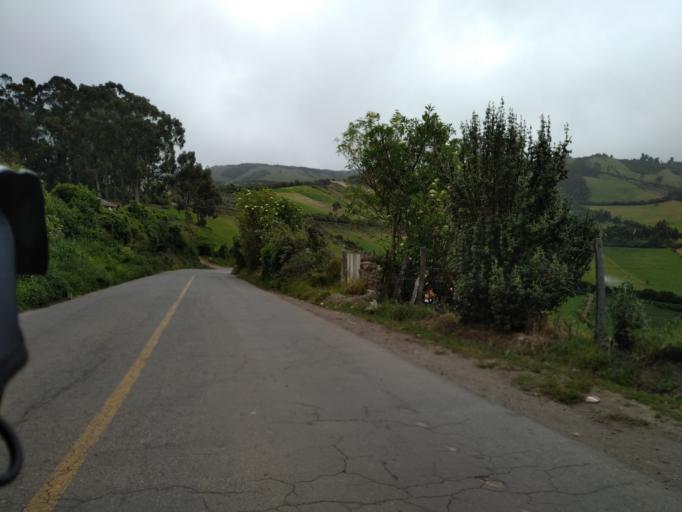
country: EC
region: Carchi
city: El Angel
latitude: 0.6334
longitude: -77.9340
